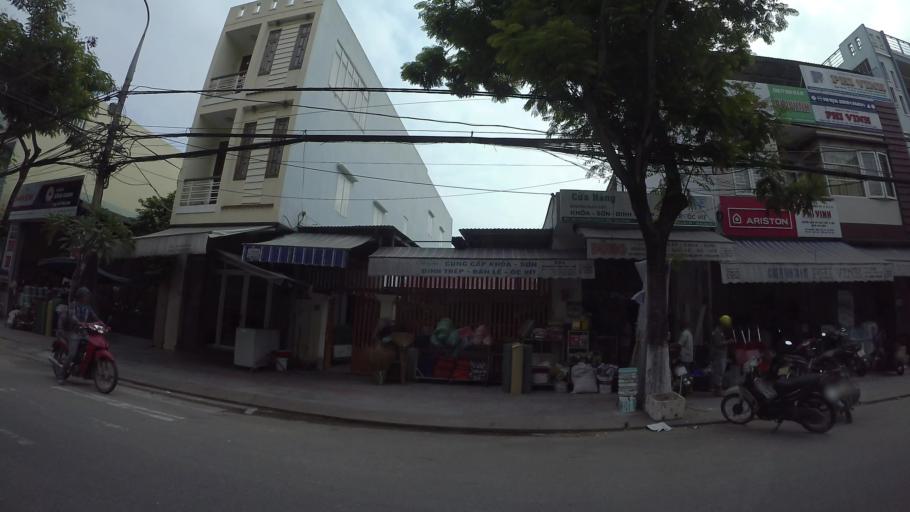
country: VN
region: Da Nang
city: Son Tra
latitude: 16.0650
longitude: 108.2408
